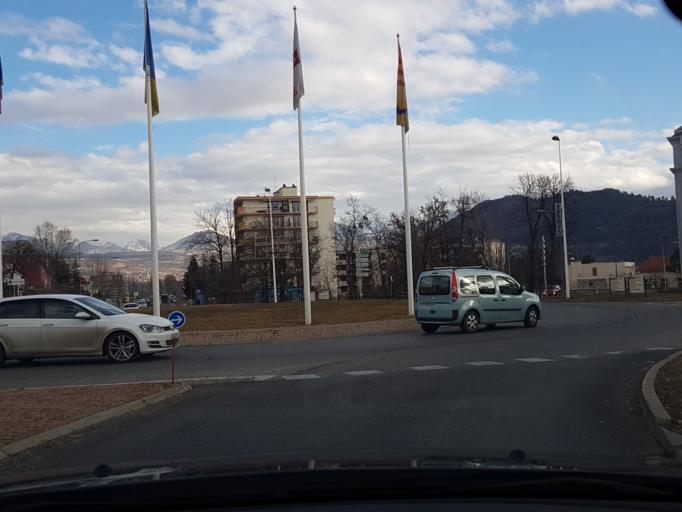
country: FR
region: Provence-Alpes-Cote d'Azur
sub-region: Departement des Hautes-Alpes
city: Gap
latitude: 44.5454
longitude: 6.0631
